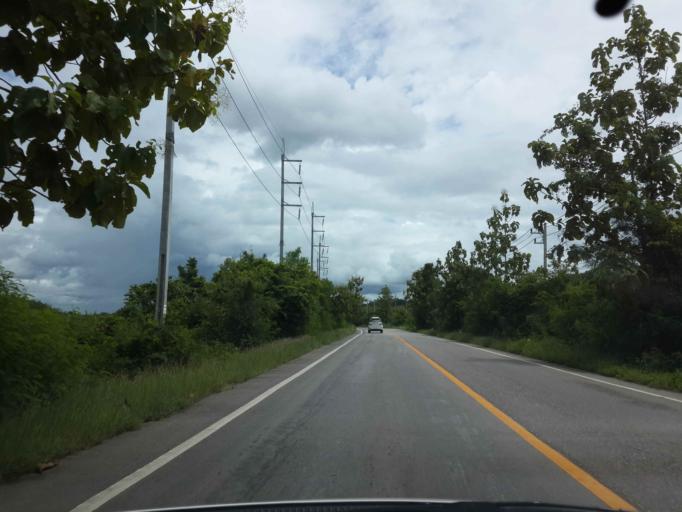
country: TH
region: Ratchaburi
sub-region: Amphoe Chom Bueng
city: Chom Bueng
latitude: 13.5590
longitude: 99.5188
